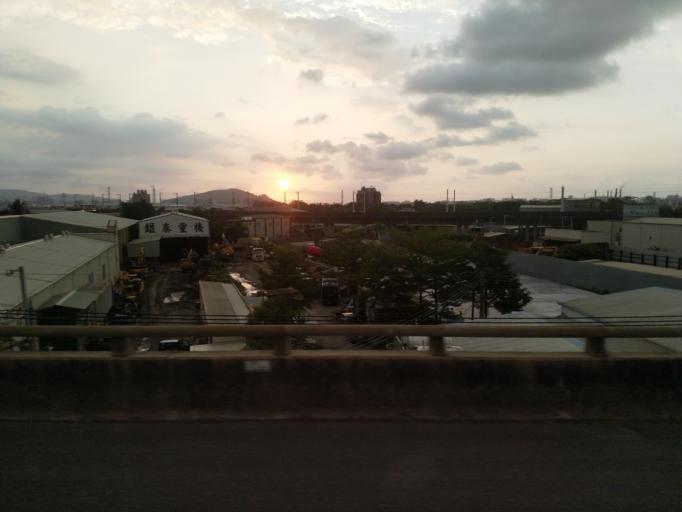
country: TW
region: Taiwan
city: Fengshan
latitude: 22.7132
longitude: 120.3601
